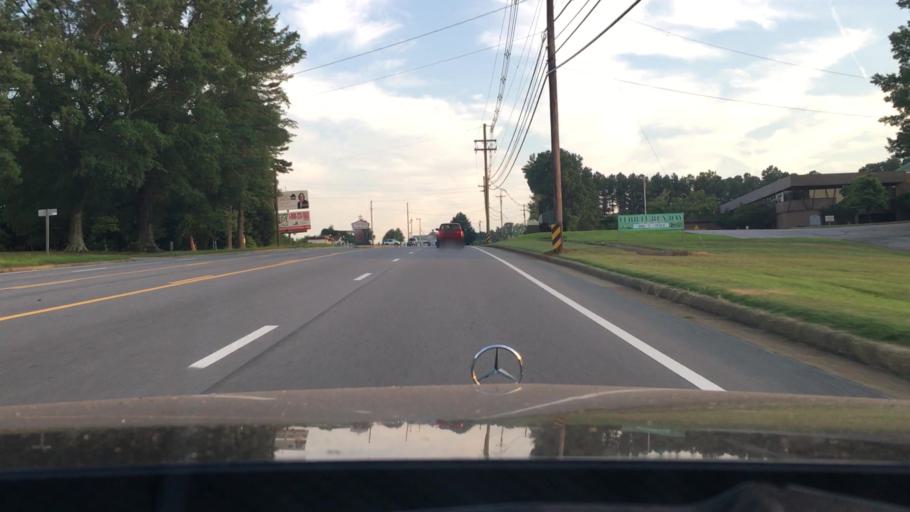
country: US
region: Virginia
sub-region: Pittsylvania County
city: Mount Hermon
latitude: 36.6442
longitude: -79.3819
